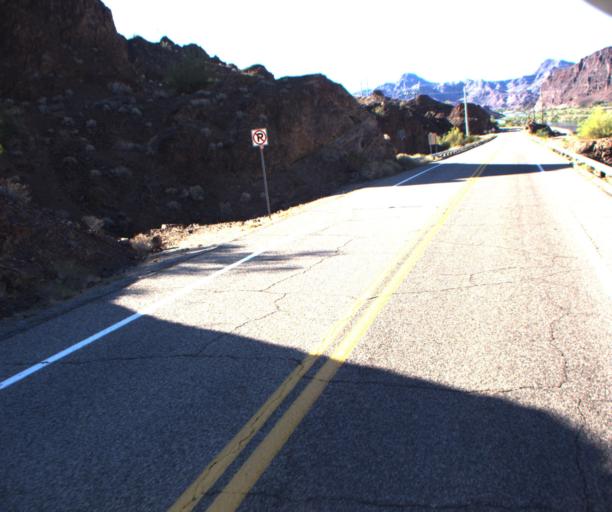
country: US
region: Arizona
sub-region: La Paz County
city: Cienega Springs
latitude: 34.2945
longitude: -114.1379
